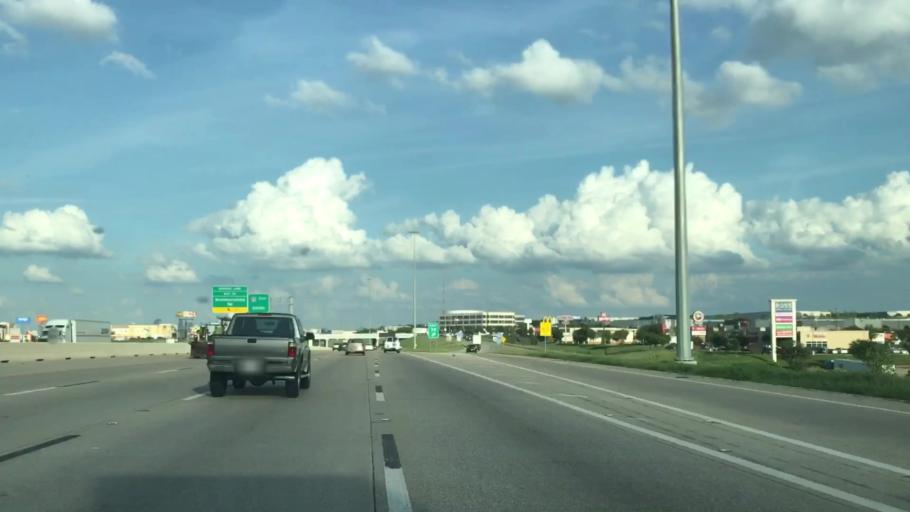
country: US
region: Texas
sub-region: Dallas County
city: Cockrell Hill
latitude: 32.7663
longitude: -96.9015
